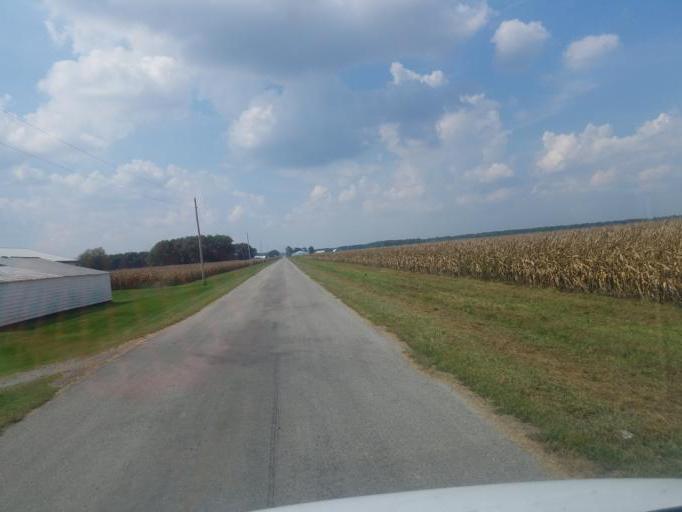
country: US
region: Ohio
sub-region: Hardin County
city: Ada
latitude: 40.6377
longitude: -83.8076
